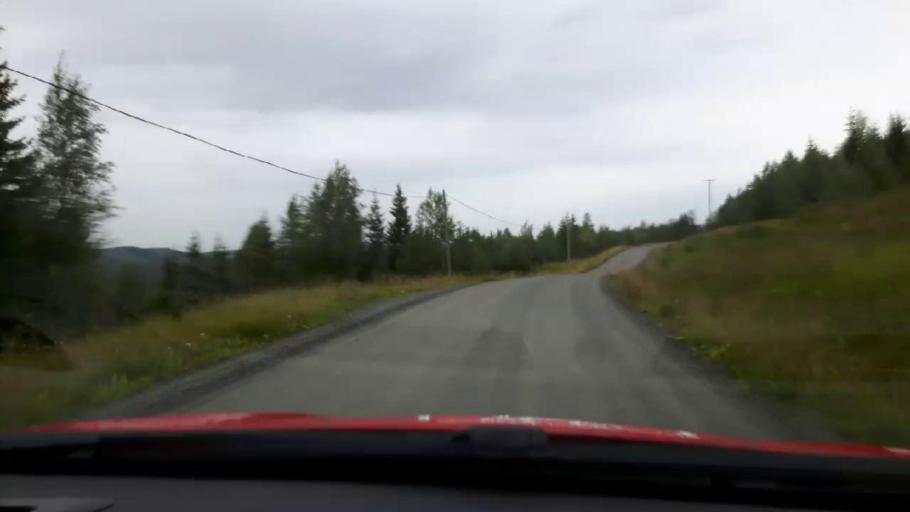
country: SE
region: Jaemtland
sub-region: Are Kommun
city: Are
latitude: 63.4119
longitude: 12.8288
